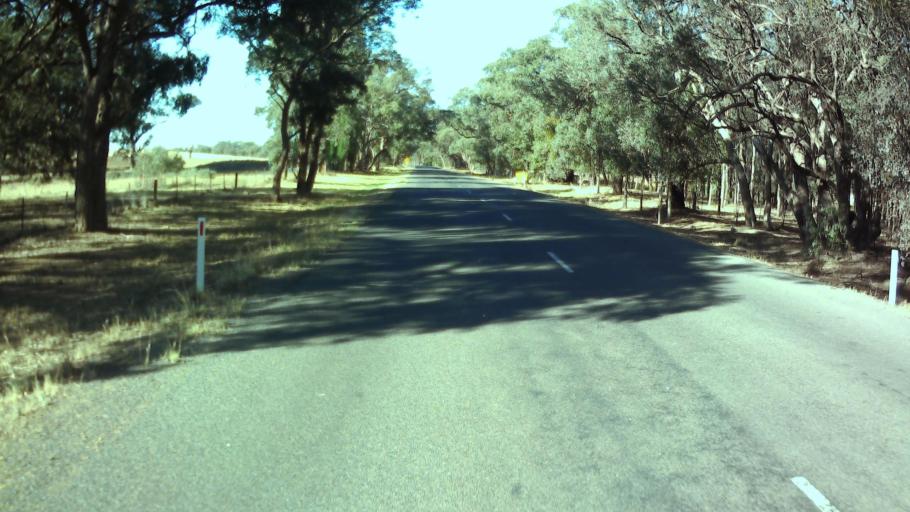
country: AU
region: New South Wales
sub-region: Weddin
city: Grenfell
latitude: -33.9907
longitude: 148.1368
